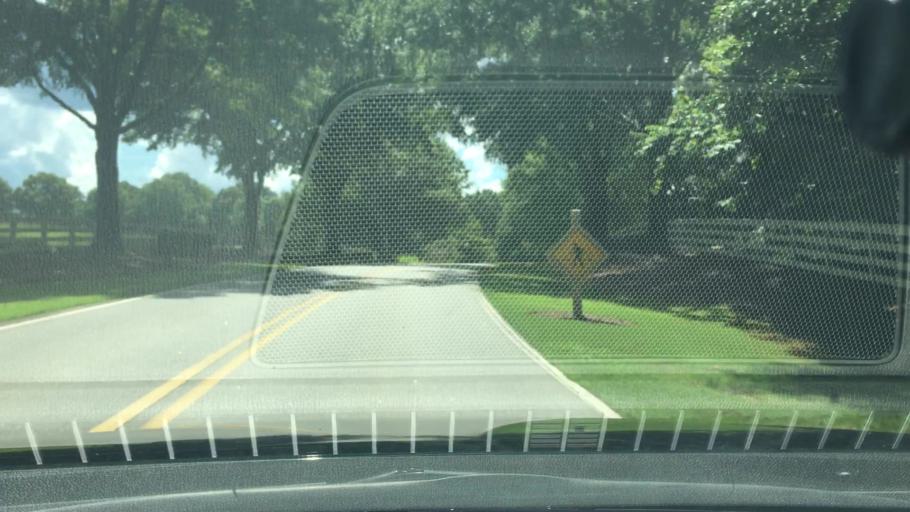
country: US
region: Georgia
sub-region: Putnam County
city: Jefferson
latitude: 33.3848
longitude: -83.2526
